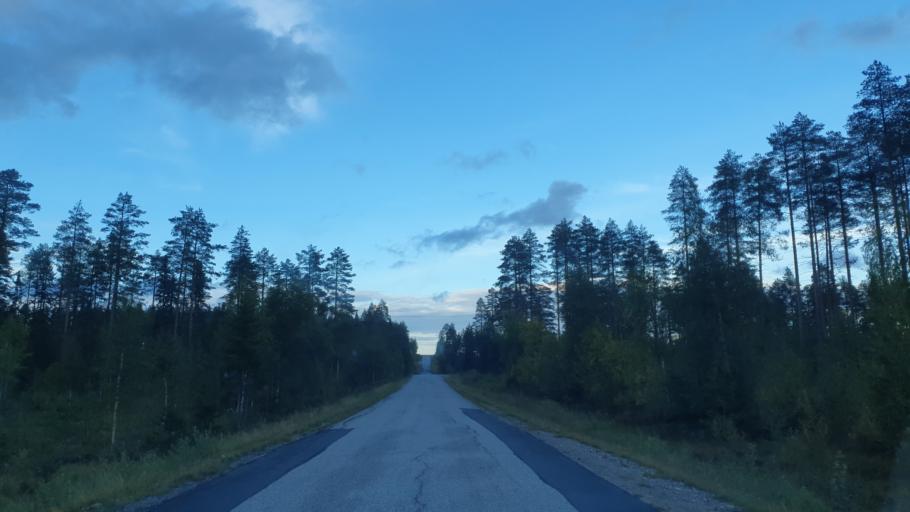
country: FI
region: Kainuu
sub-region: Kehys-Kainuu
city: Kuhmo
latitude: 64.3999
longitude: 29.8659
